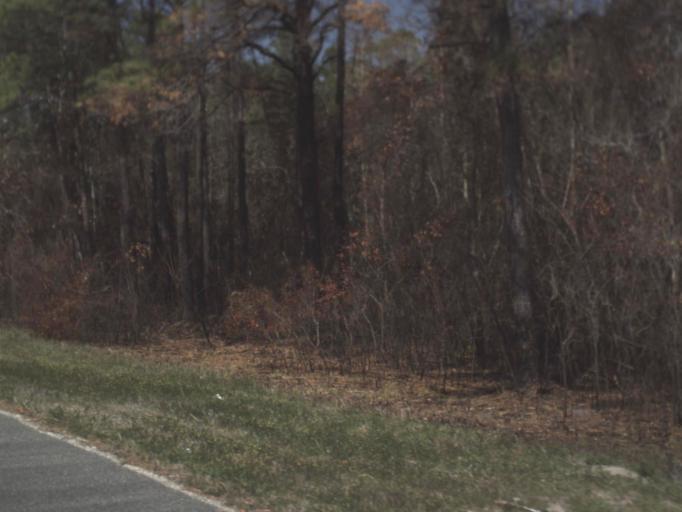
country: US
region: Florida
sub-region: Gadsden County
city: Midway
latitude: 30.3519
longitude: -84.5161
